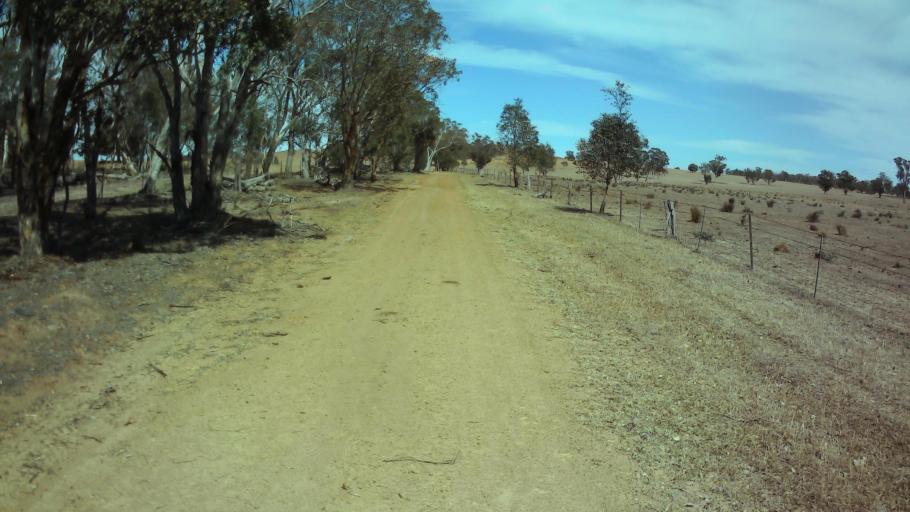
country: AU
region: New South Wales
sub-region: Weddin
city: Grenfell
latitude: -33.6810
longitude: 148.2743
